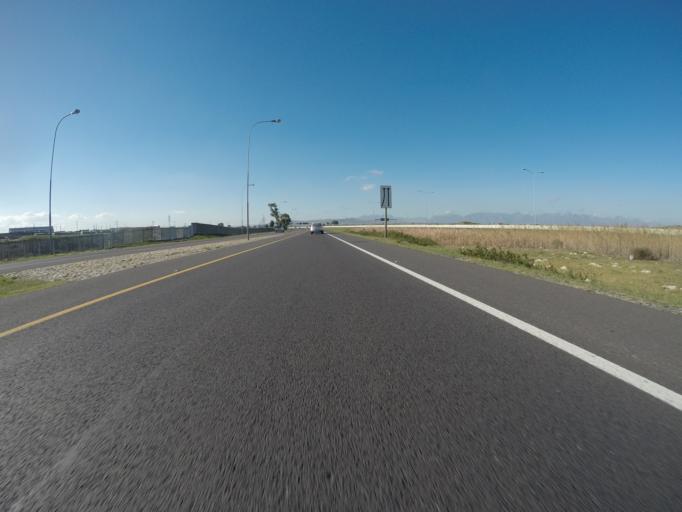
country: ZA
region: Western Cape
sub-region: City of Cape Town
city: Lansdowne
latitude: -33.9976
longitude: 18.6359
